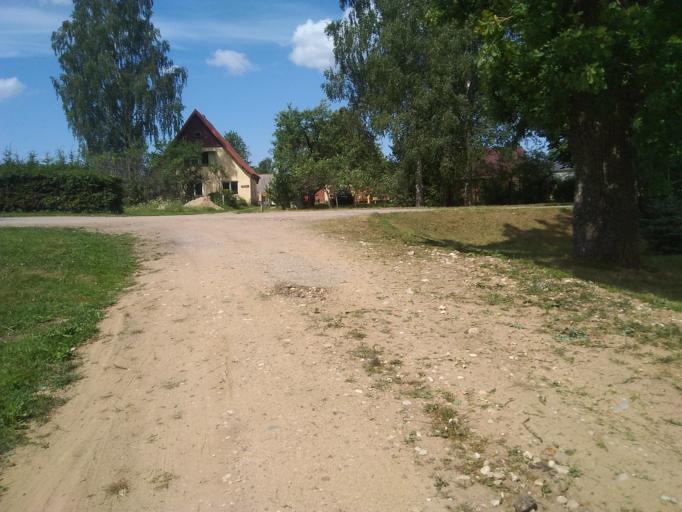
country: LV
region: Pargaujas
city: Stalbe
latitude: 57.3565
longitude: 24.9538
